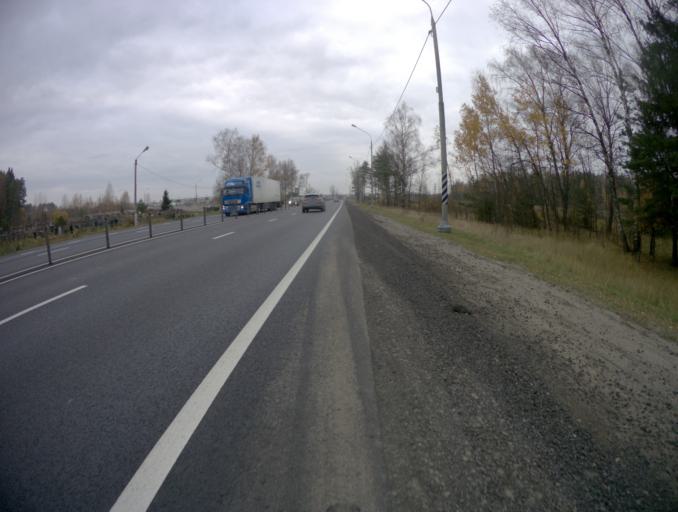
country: RU
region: Moskovskaya
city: Malaya Dubna
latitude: 55.8693
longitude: 38.9640
